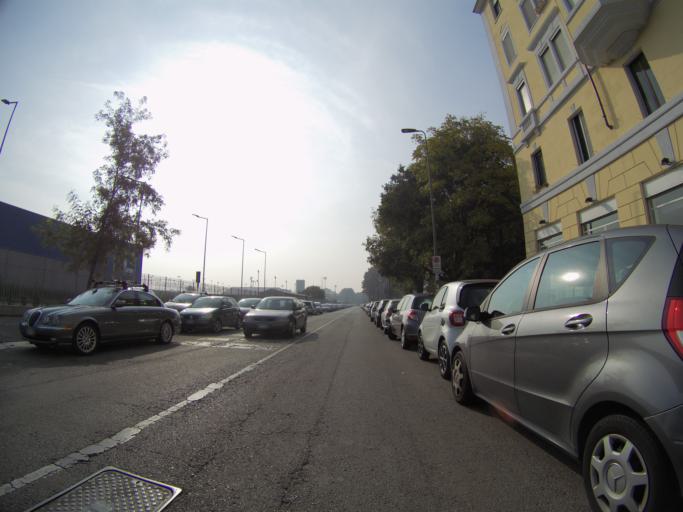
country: IT
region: Lombardy
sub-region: Citta metropolitana di Milano
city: Novegro-Tregarezzo-San Felice
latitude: 45.4794
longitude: 9.2366
